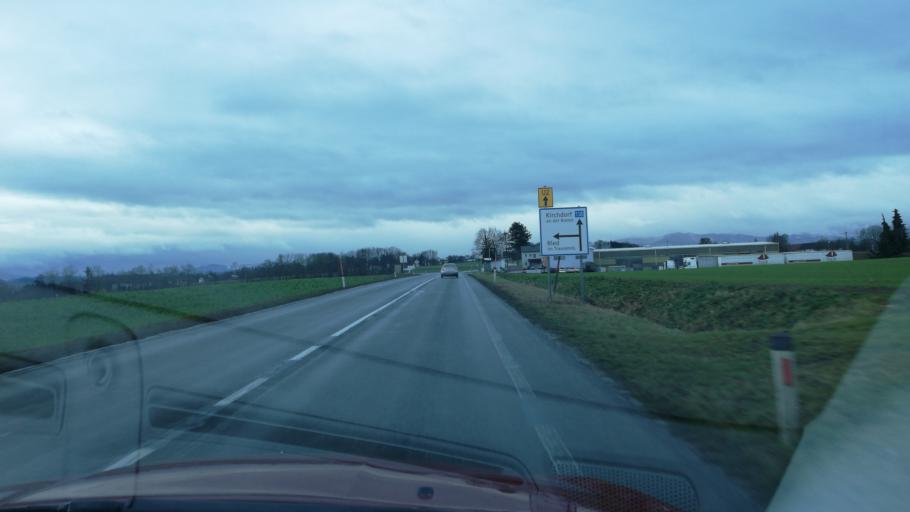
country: AT
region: Upper Austria
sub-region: Wels-Land
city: Sattledt
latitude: 48.0293
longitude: 14.0583
